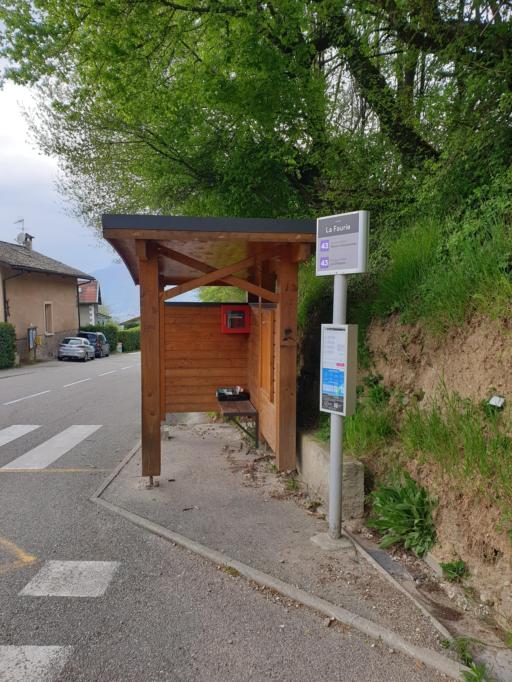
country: FR
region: Rhone-Alpes
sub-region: Departement de l'Isere
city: Gieres
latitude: 45.1752
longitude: 5.7950
